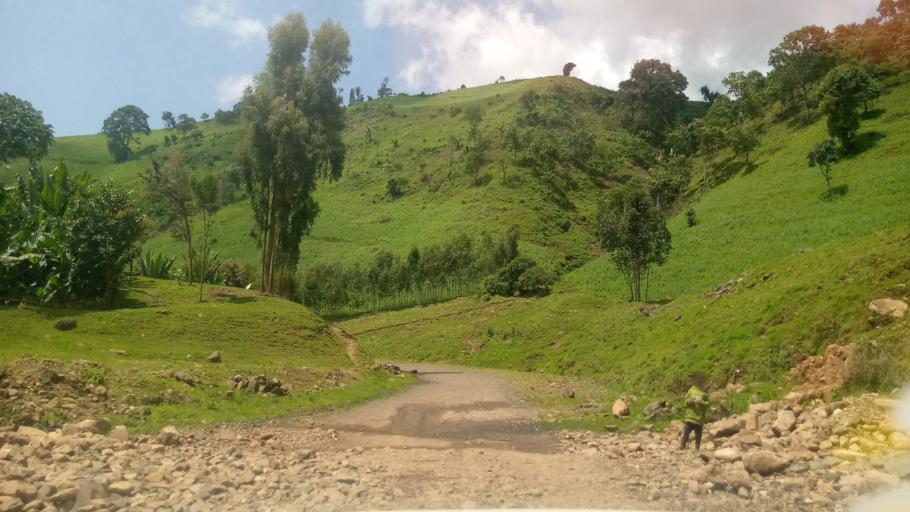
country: ET
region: Southern Nations, Nationalities, and People's Region
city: Bonga
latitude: 7.1469
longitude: 36.5719
